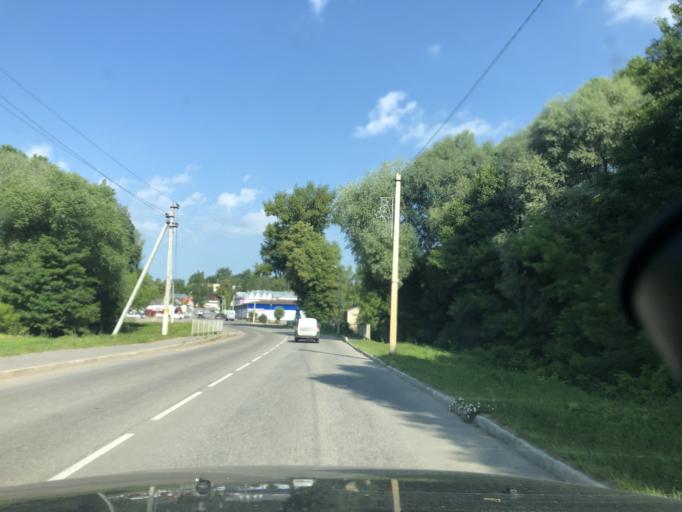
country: RU
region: Tula
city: Dubna
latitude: 54.1502
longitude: 36.9678
